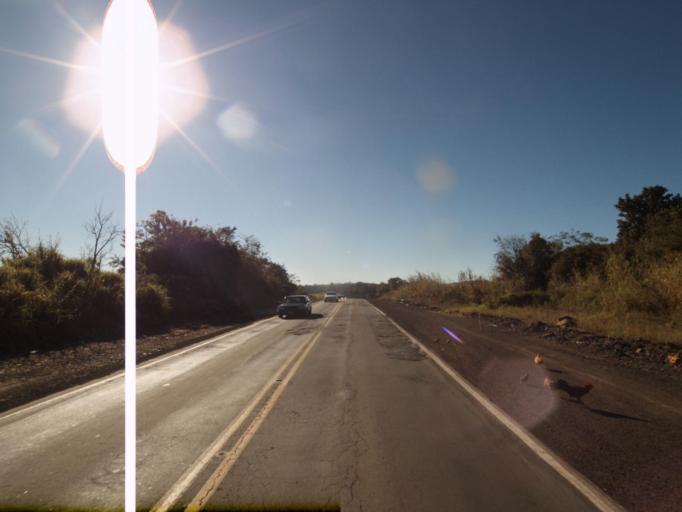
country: AR
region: Misiones
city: Bernardo de Irigoyen
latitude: -26.6504
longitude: -53.5185
